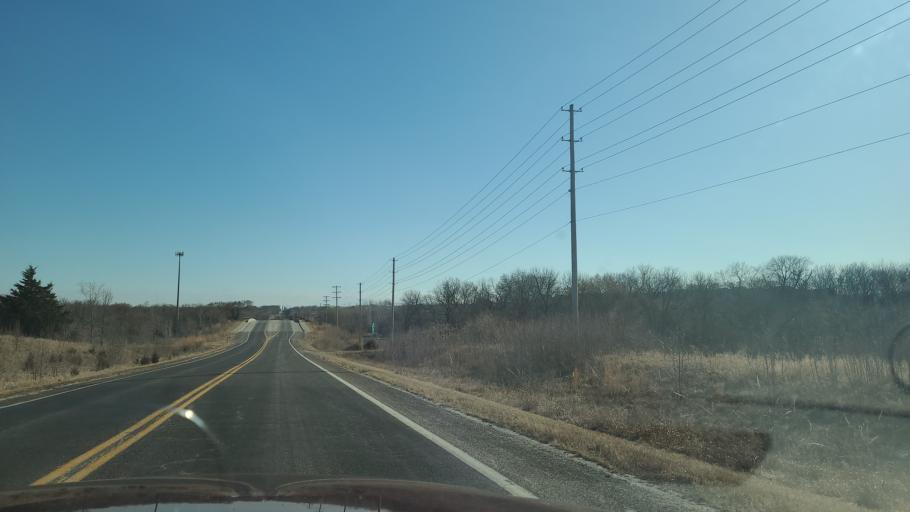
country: US
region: Kansas
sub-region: Douglas County
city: Lawrence
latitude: 38.9980
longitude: -95.2792
